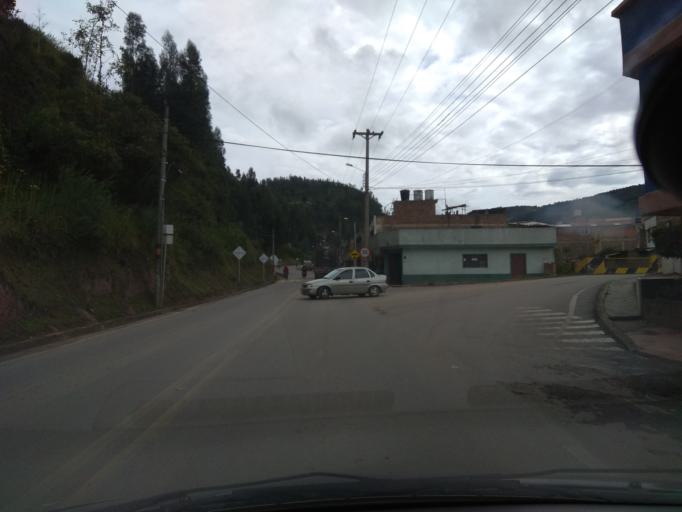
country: CO
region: Boyaca
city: Duitama
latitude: 5.8363
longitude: -73.0204
